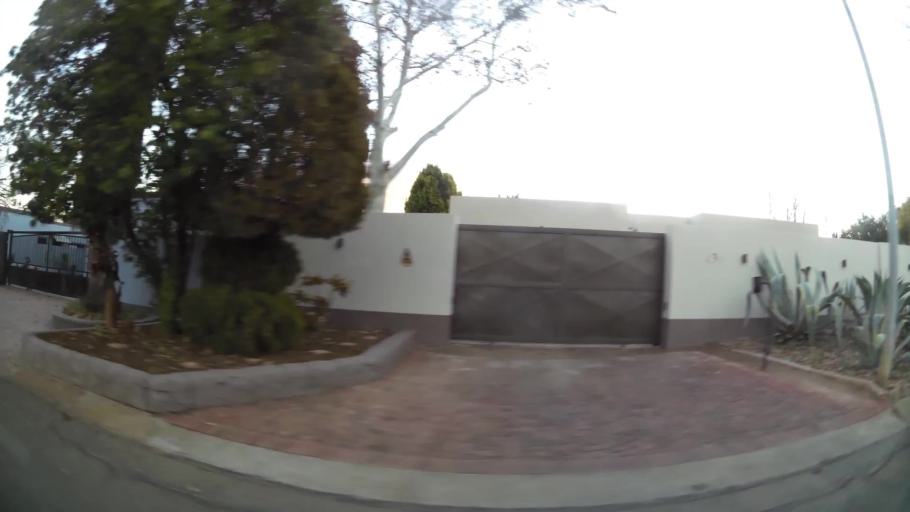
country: ZA
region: North-West
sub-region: Dr Kenneth Kaunda District Municipality
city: Potchefstroom
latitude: -26.7208
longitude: 27.1230
